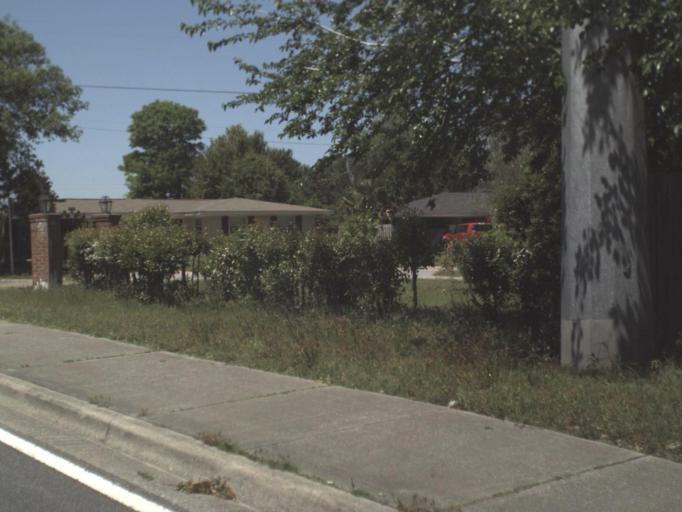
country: US
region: Florida
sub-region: Escambia County
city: Ferry Pass
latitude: 30.4951
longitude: -87.1874
